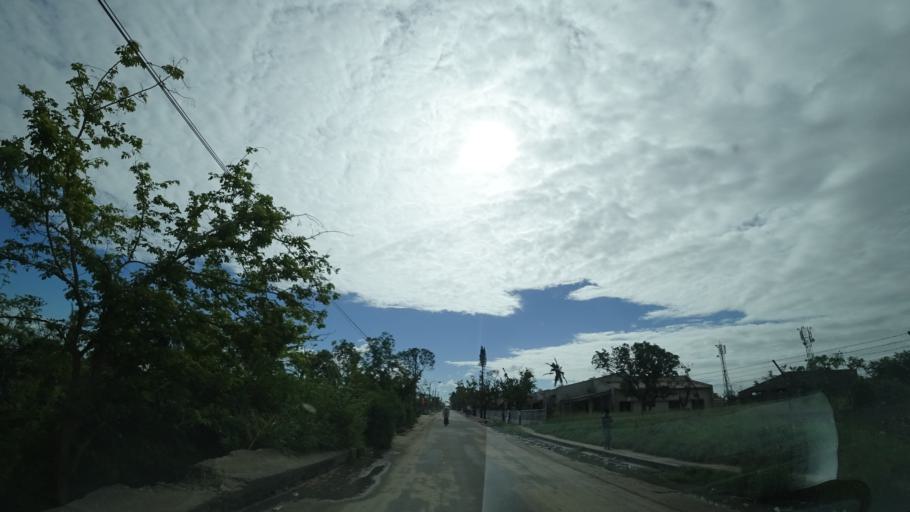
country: MZ
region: Sofala
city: Beira
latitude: -19.8007
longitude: 34.8990
